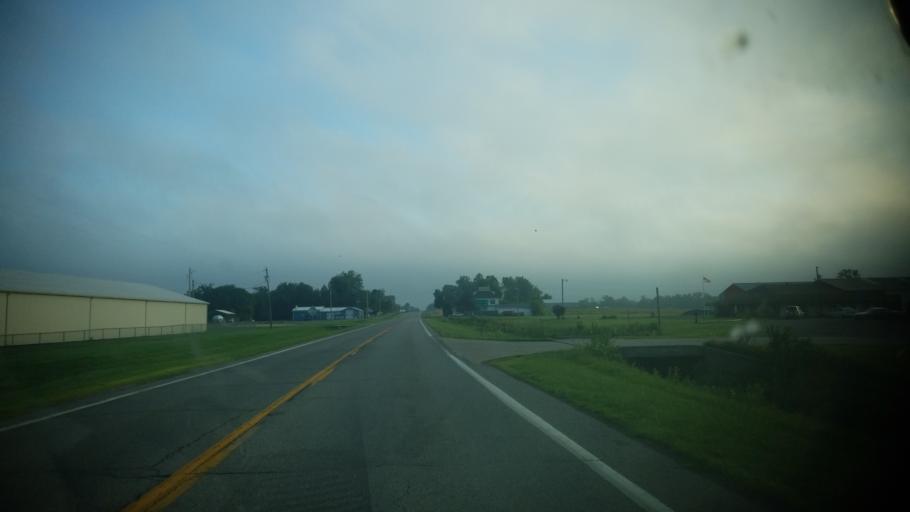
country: US
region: Illinois
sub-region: Wayne County
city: Fairfield
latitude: 38.3816
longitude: -88.4058
